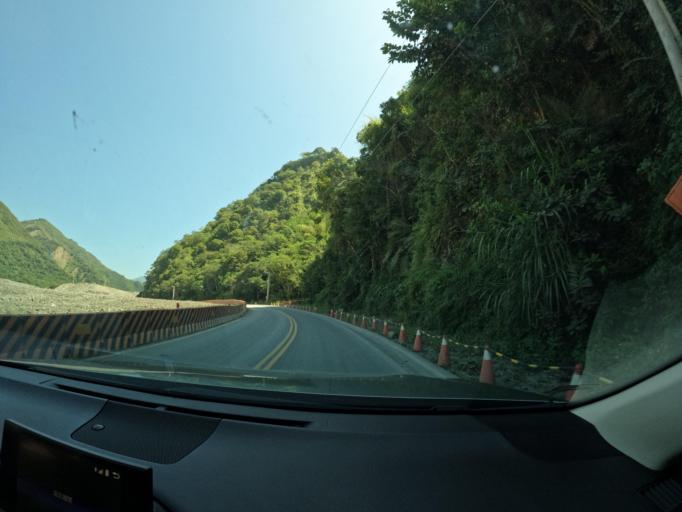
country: TW
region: Taiwan
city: Yujing
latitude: 23.1834
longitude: 120.7823
